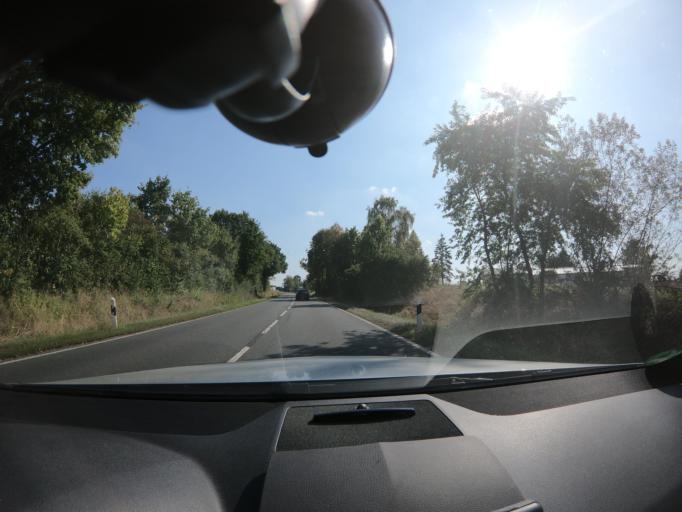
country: DE
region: Hesse
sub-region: Regierungsbezirk Giessen
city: Kirchhain
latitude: 50.8327
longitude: 8.9205
